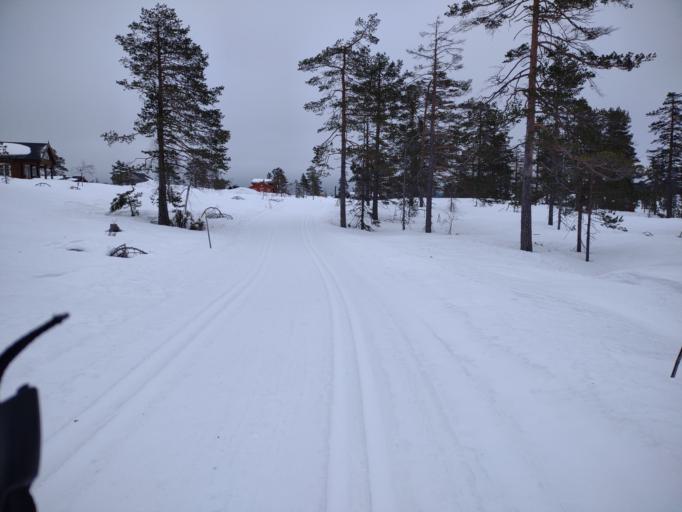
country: NO
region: Buskerud
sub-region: Flesberg
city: Lampeland
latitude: 59.7951
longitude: 9.4376
